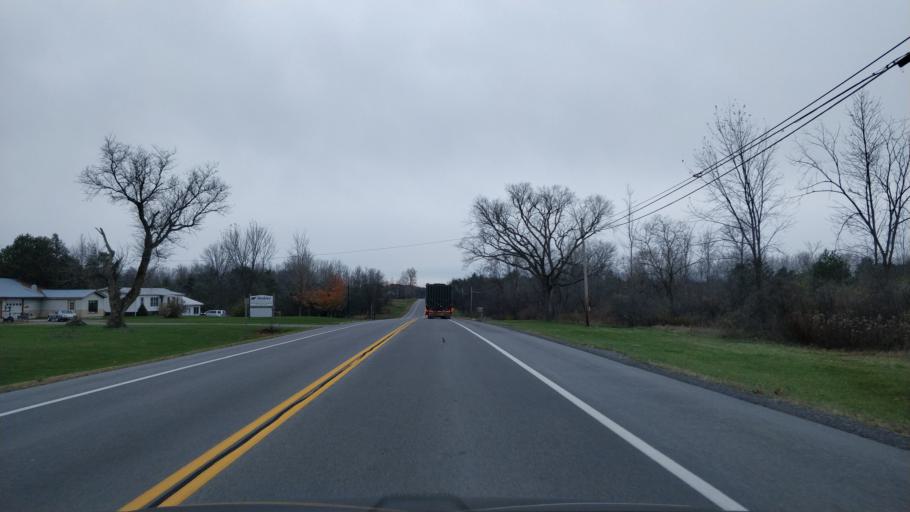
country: CA
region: Ontario
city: Brockville
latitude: 44.6222
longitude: -75.5918
